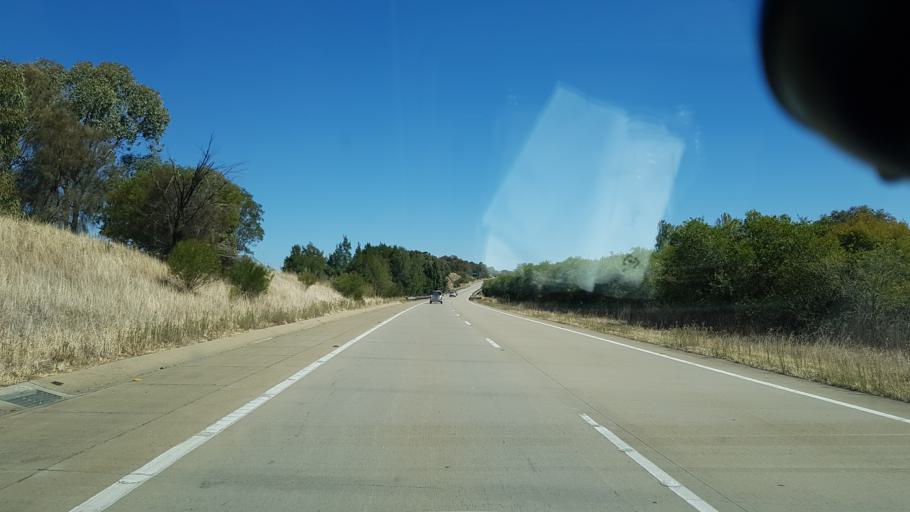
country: AU
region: New South Wales
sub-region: Gundagai
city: Gundagai
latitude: -34.8195
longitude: 148.3769
